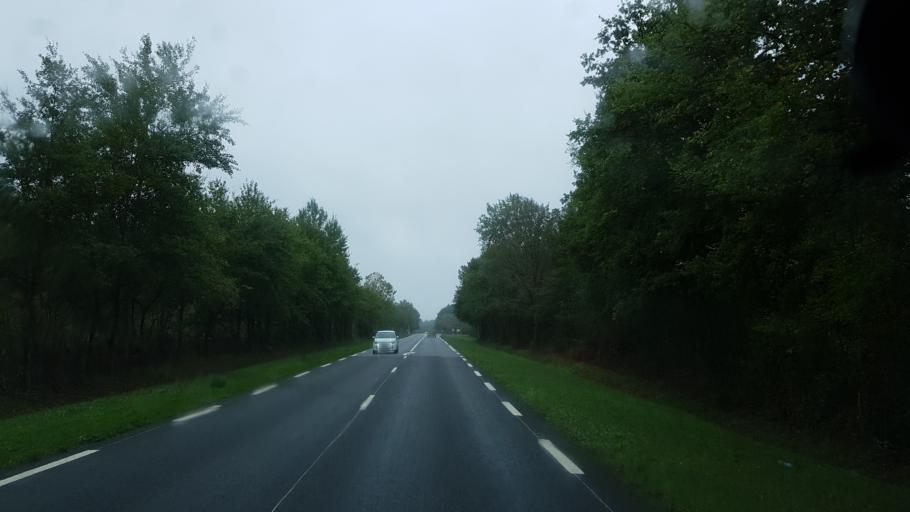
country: FR
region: Centre
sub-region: Departement du Loir-et-Cher
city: Salbris
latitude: 47.4600
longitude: 2.0421
